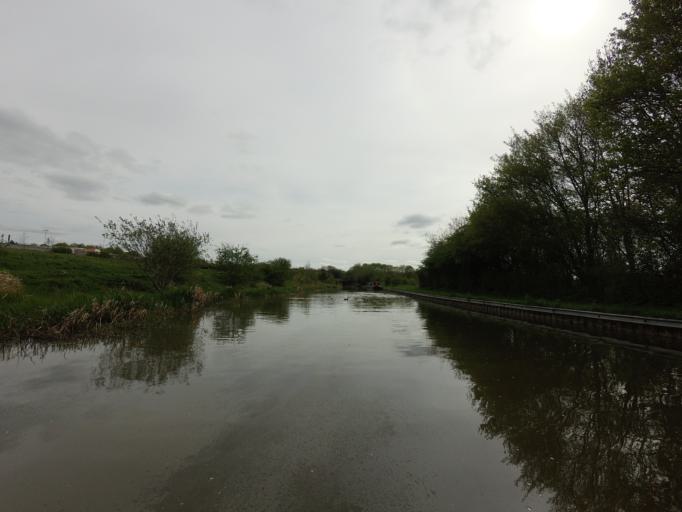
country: GB
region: England
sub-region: Milton Keynes
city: Bradwell
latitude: 52.0693
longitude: -0.7801
